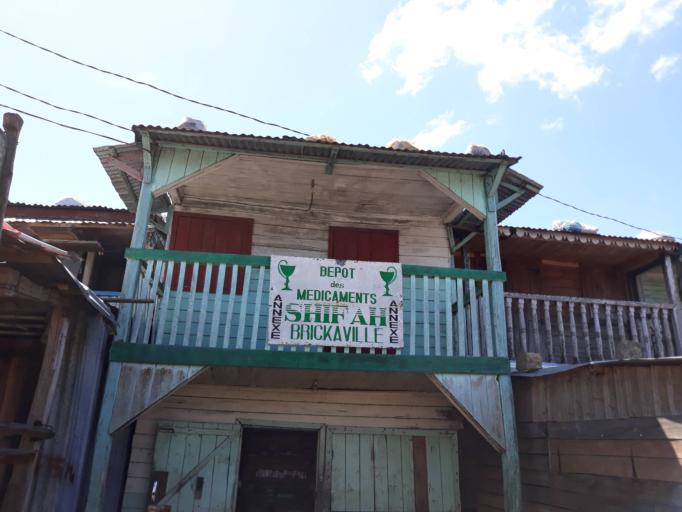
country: MG
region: Atsinanana
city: Ampasimanolotra
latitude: -18.8214
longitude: 49.0714
